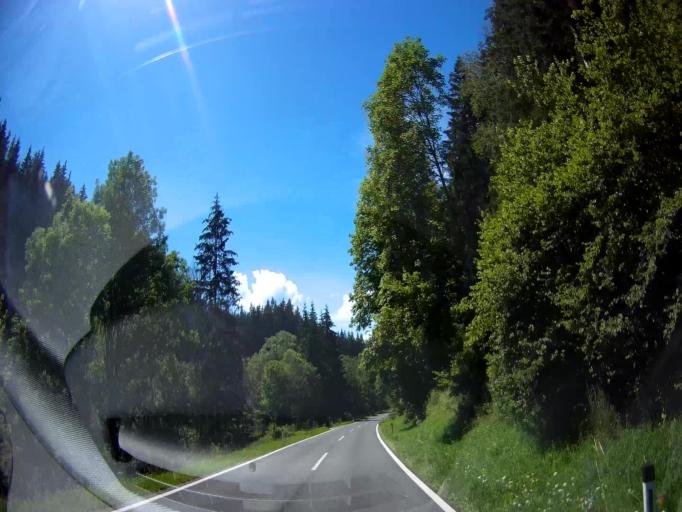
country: AT
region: Carinthia
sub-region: Politischer Bezirk Sankt Veit an der Glan
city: Glodnitz
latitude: 46.8508
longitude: 14.1450
